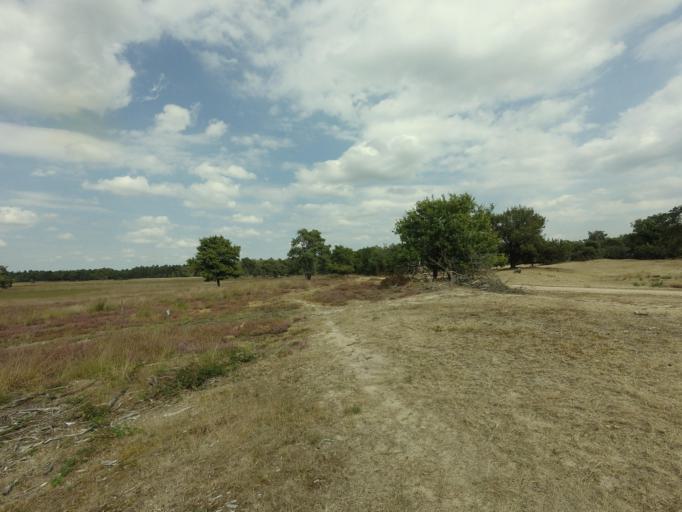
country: NL
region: North Brabant
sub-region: Gemeente Someren
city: Someren
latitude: 51.3980
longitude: 5.6612
